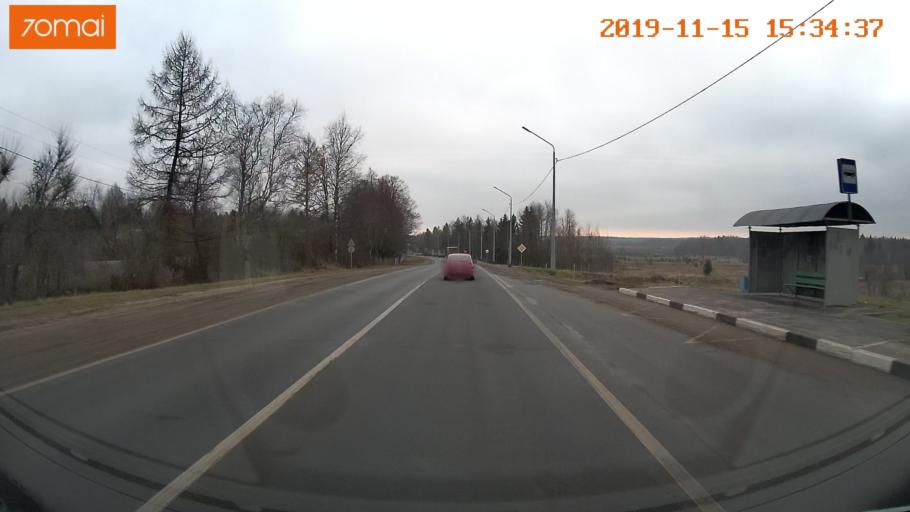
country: RU
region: Jaroslavl
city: Danilov
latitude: 58.0676
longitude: 40.0885
